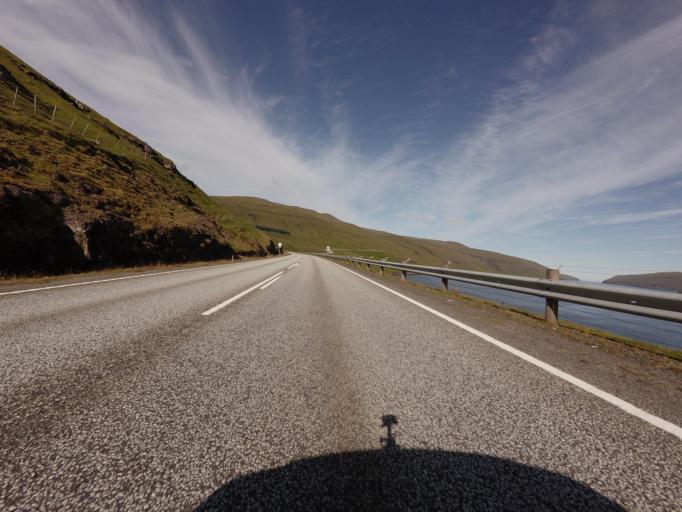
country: FO
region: Streymoy
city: Vestmanna
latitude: 62.1004
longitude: -7.1273
